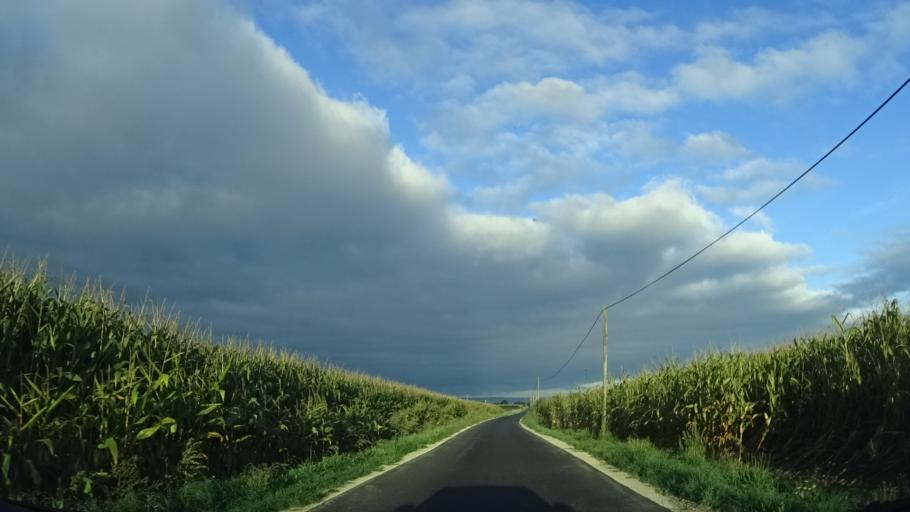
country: FR
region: Brittany
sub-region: Departement du Finistere
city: Lampaul-Plouarzel
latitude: 48.4579
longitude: -4.7419
